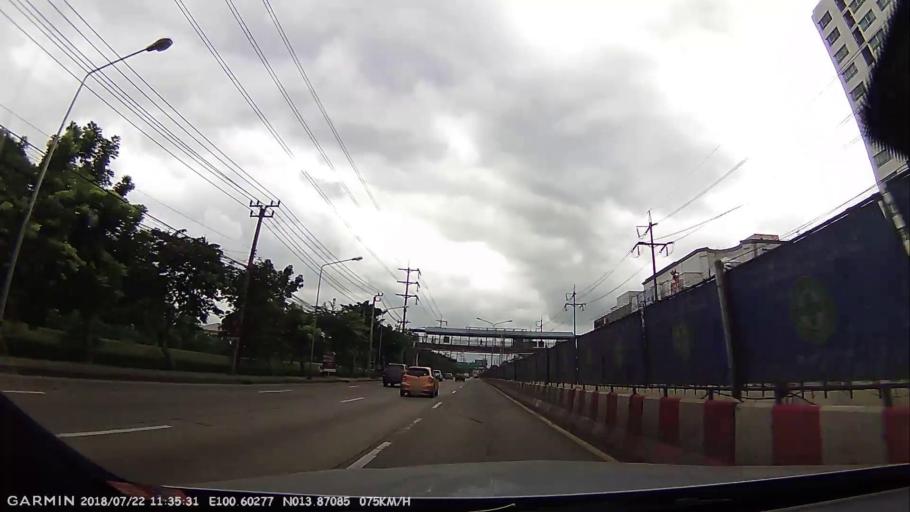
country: TH
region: Bangkok
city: Bang Khen
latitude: 13.8709
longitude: 100.6027
